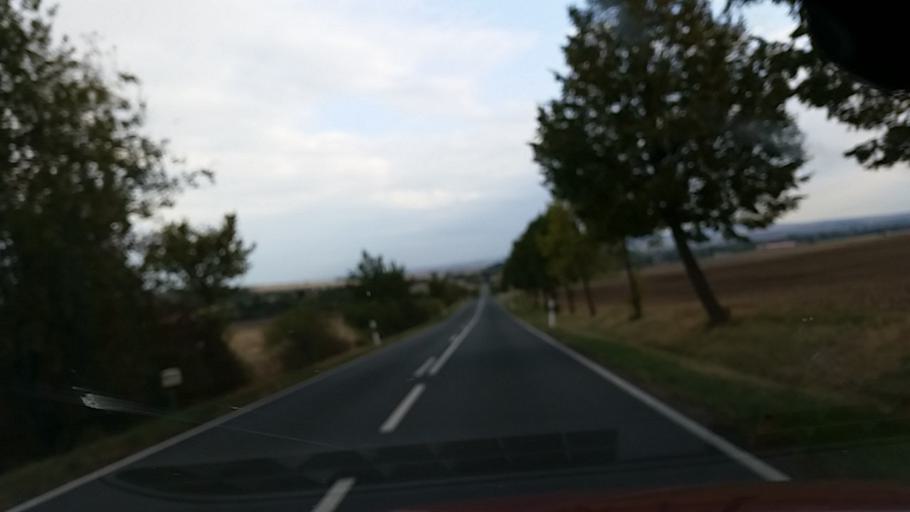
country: DE
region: Thuringia
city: Beichlingen
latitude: 51.2169
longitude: 11.2541
